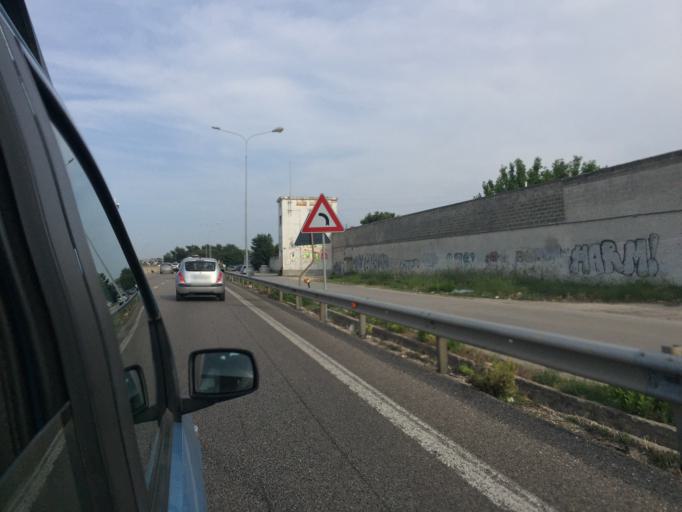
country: IT
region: Apulia
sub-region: Provincia di Bari
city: Triggiano
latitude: 41.0946
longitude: 16.9458
